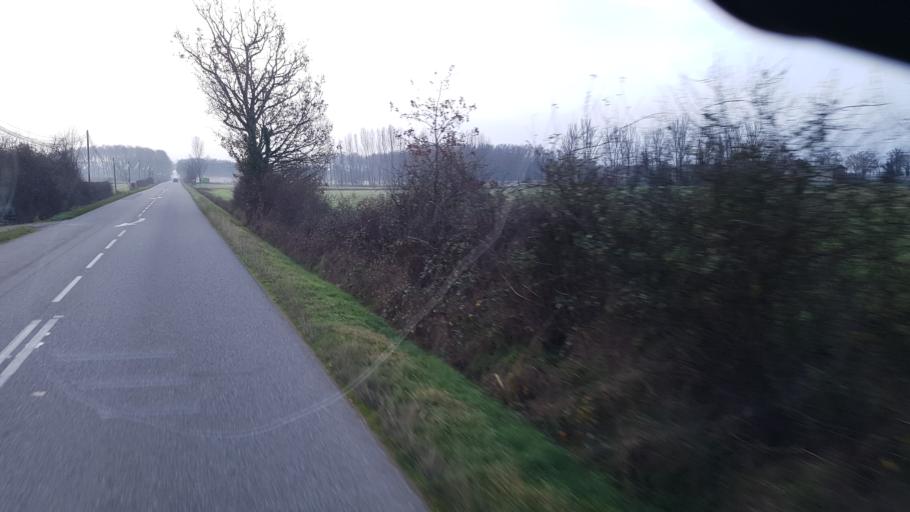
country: FR
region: Midi-Pyrenees
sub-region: Departement du Tarn-et-Garonne
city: Montricoux
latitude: 44.0978
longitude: 1.6030
